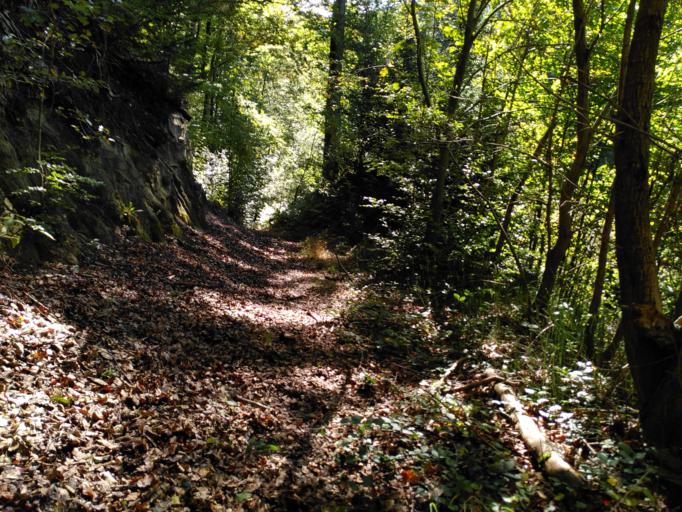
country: CH
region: Bern
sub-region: Oberaargau
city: Seeberg
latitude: 47.1315
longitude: 7.7050
